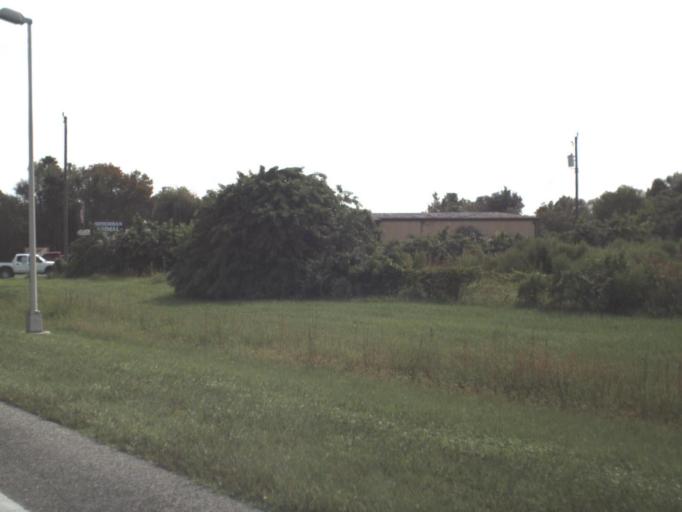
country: US
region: Florida
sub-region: Lee County
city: Fort Myers Shores
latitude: 26.6968
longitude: -81.7751
